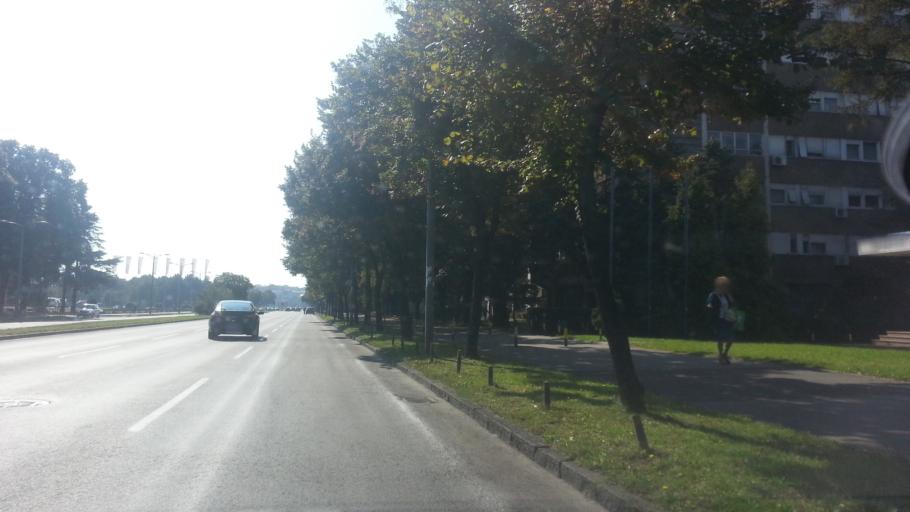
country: RS
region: Central Serbia
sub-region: Belgrade
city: Zemun
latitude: 44.8308
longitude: 20.4189
